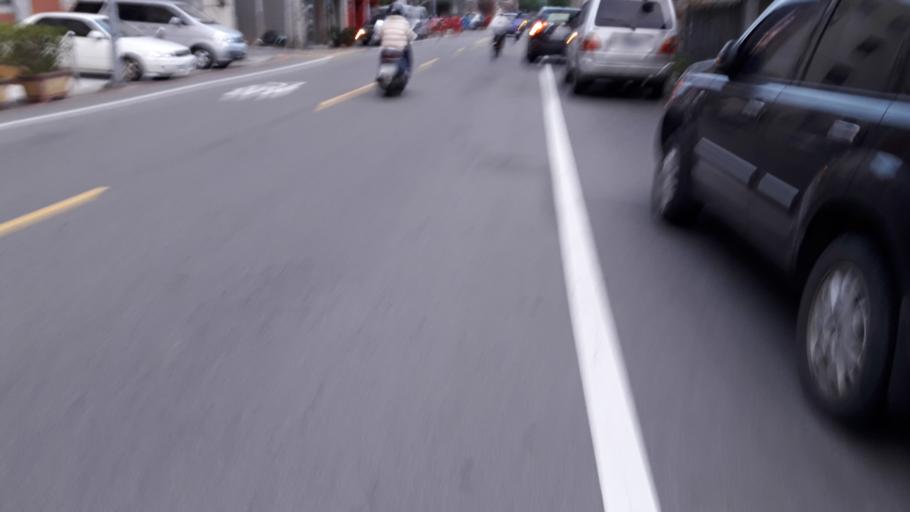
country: TW
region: Taiwan
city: Daxi
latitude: 24.8620
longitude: 121.2153
